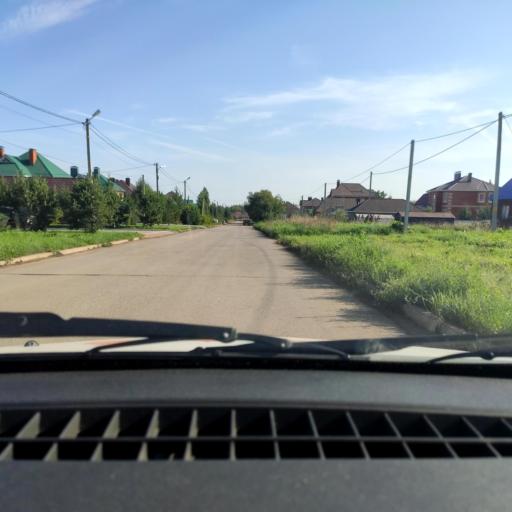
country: RU
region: Bashkortostan
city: Kabakovo
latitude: 54.6193
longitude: 56.1259
